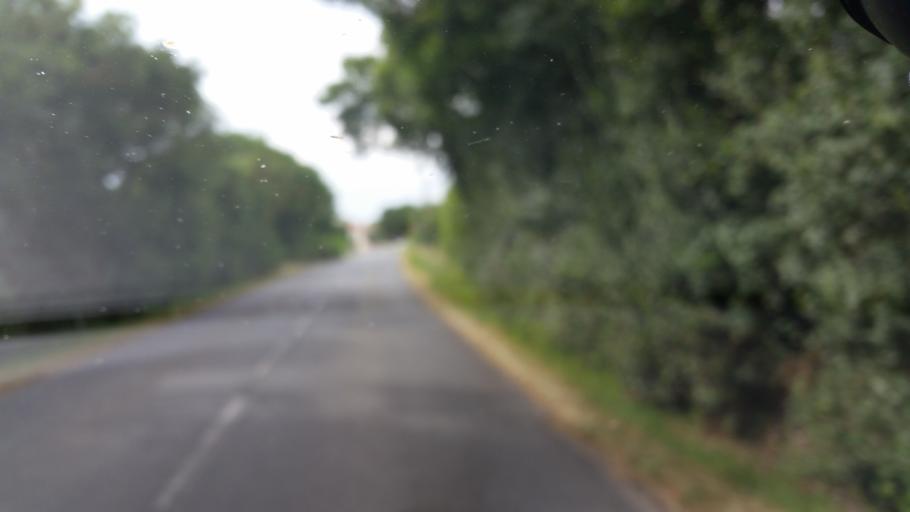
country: FR
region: Poitou-Charentes
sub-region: Departement de la Charente-Maritime
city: Saint-Jean-de-Liversay
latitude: 46.2140
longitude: -0.8814
